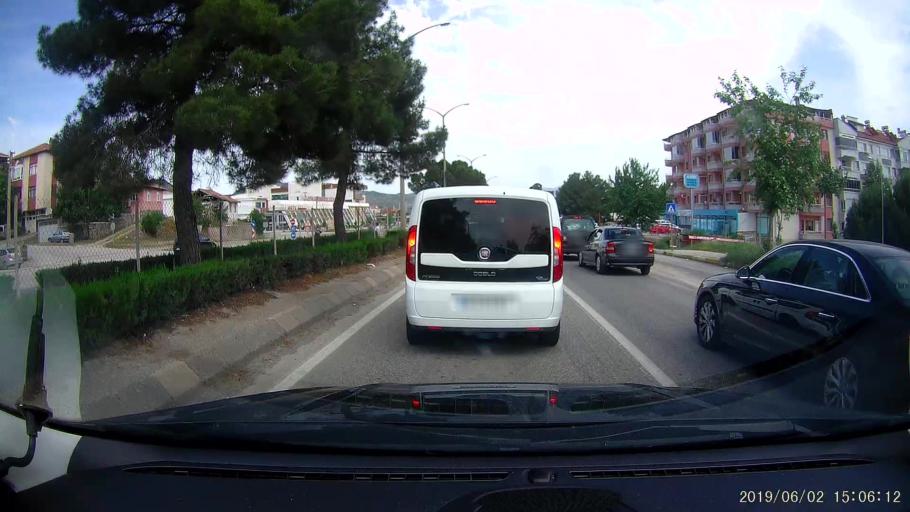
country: TR
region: Corum
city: Osmancik
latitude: 40.9795
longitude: 34.8014
